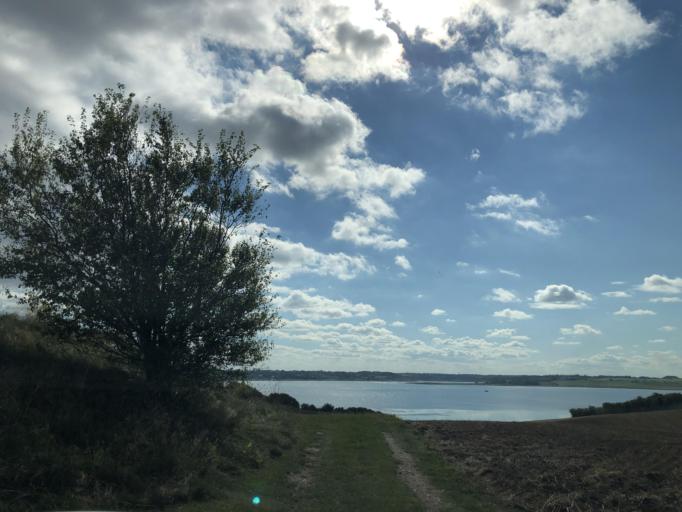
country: DK
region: Central Jutland
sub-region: Viborg Kommune
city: Viborg
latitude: 56.5560
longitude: 9.3091
